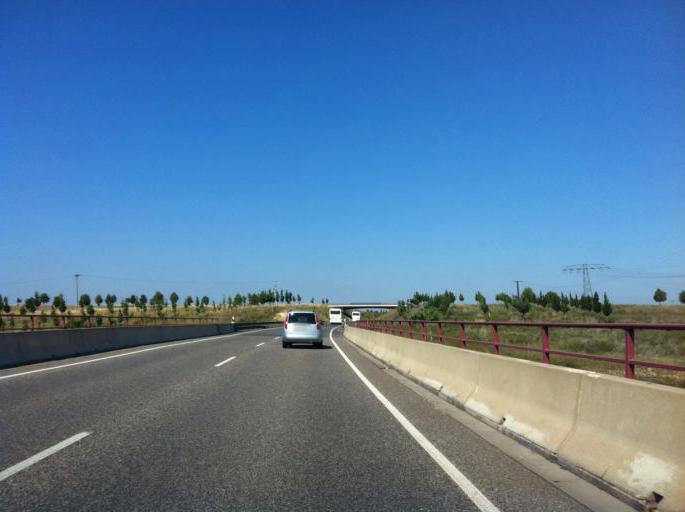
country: DE
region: Thuringia
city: Bad Langensalza
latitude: 51.0946
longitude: 10.6231
